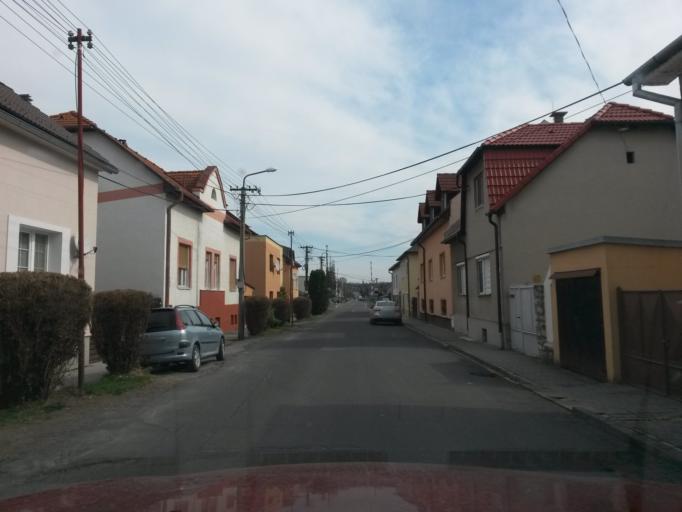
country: SK
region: Banskobystricky
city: Lucenec
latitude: 48.3305
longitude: 19.6737
